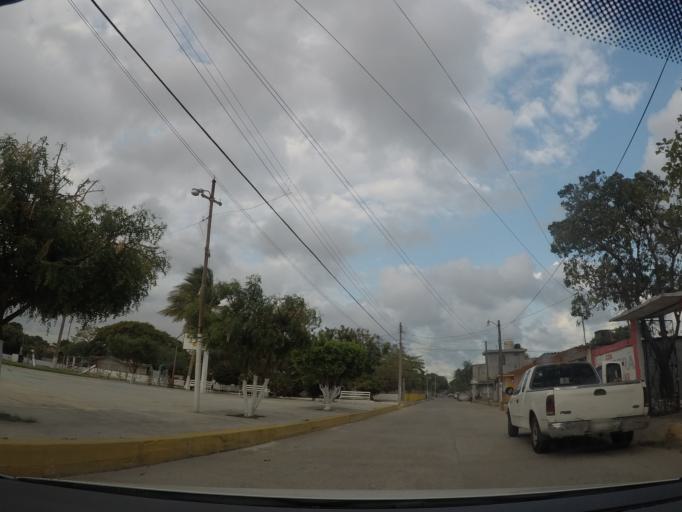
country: MX
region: Oaxaca
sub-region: Salina Cruz
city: Salina Cruz
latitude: 16.2147
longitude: -95.1985
